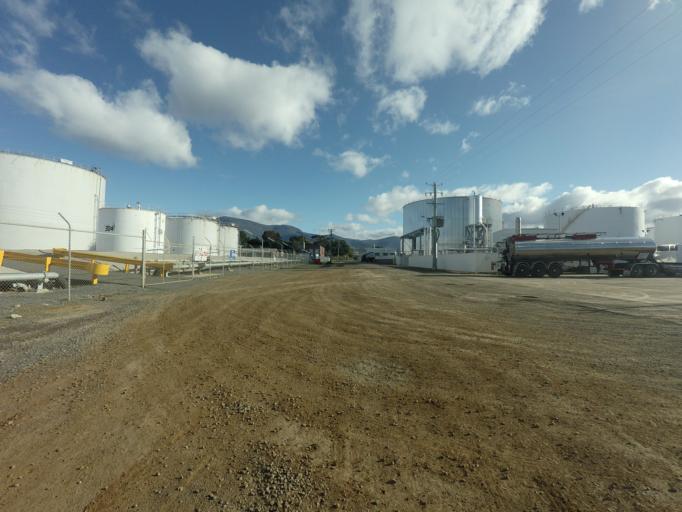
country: AU
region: Tasmania
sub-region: Glenorchy
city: Lutana
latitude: -42.8461
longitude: 147.3271
